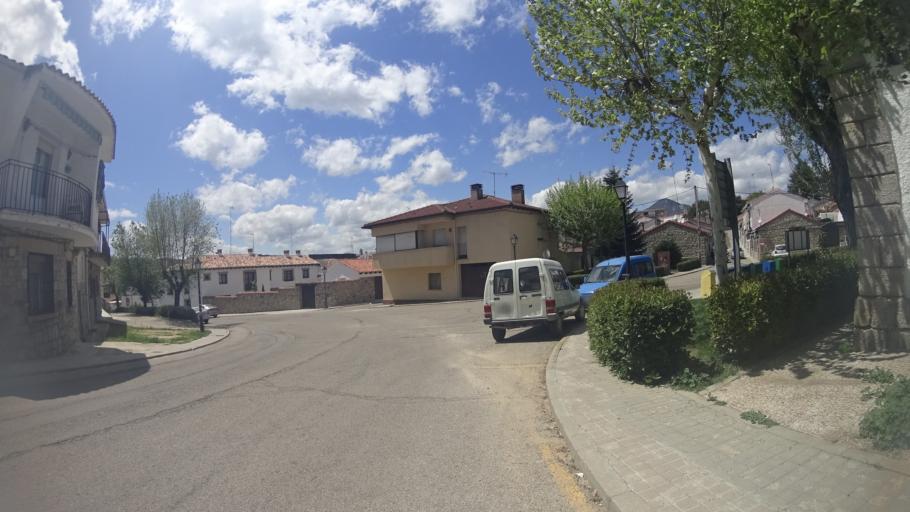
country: ES
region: Madrid
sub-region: Provincia de Madrid
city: San Martin de Valdeiglesias
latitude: 40.3624
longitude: -4.4028
